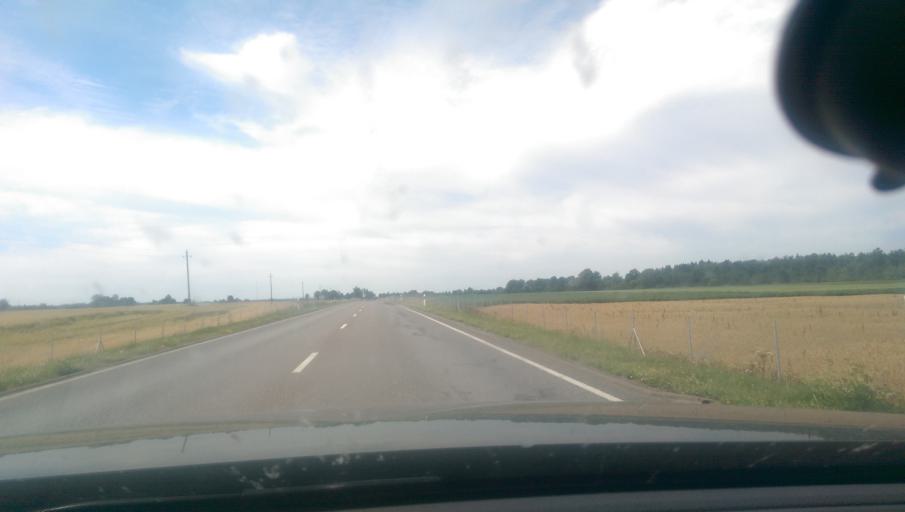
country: LT
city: Prienai
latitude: 54.6173
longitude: 23.9036
